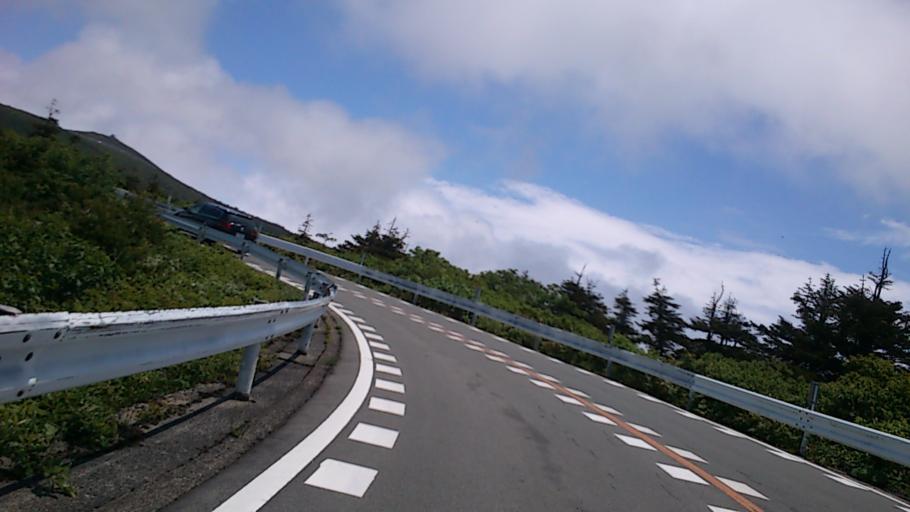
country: JP
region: Yamagata
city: Yamagata-shi
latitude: 38.1246
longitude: 140.4286
